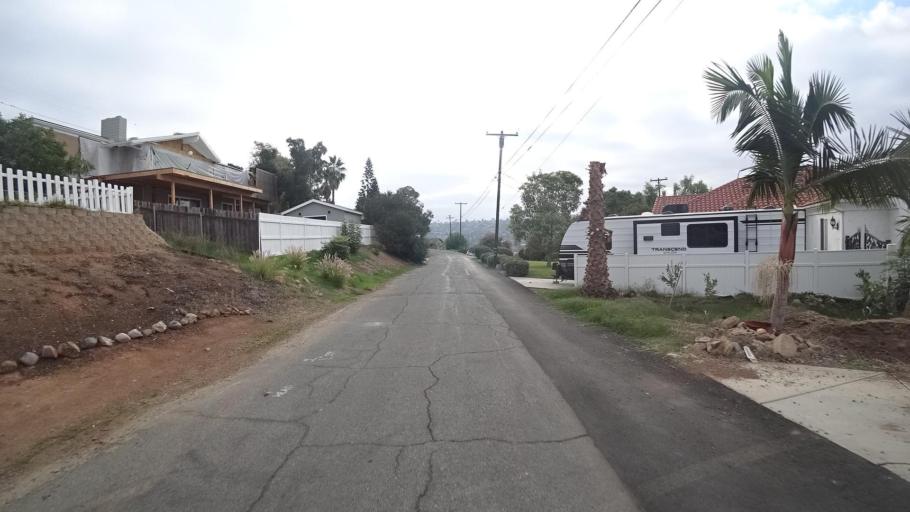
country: US
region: California
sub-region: San Diego County
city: Spring Valley
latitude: 32.7437
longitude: -117.0100
